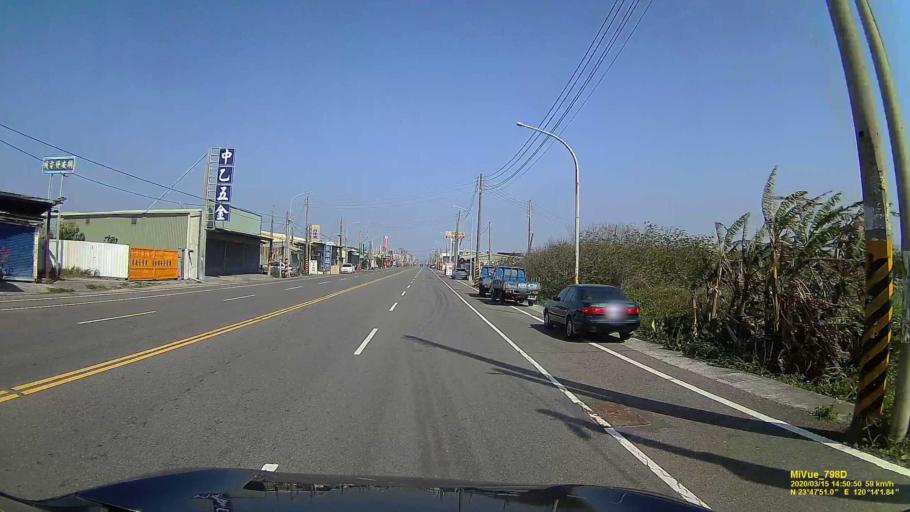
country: TW
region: Taiwan
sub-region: Yunlin
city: Douliu
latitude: 23.7975
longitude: 120.2339
